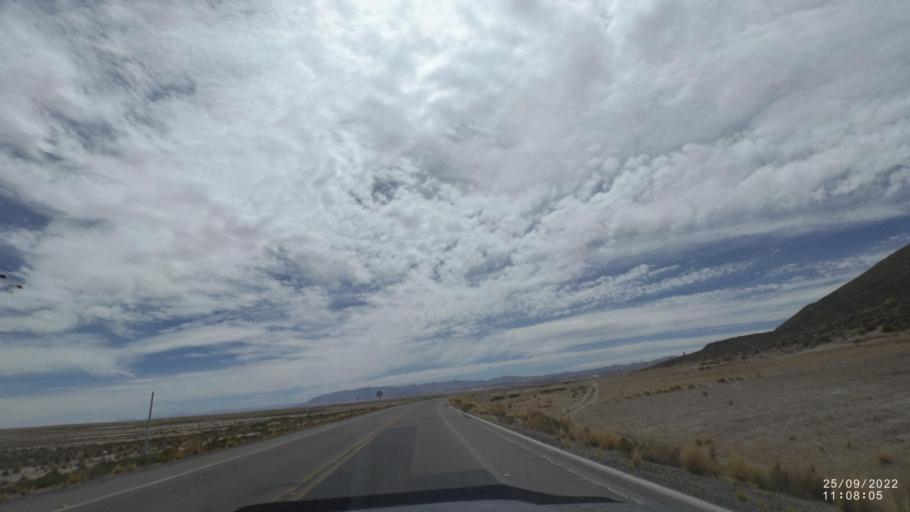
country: BO
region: Oruro
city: Challapata
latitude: -19.3329
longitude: -66.8521
